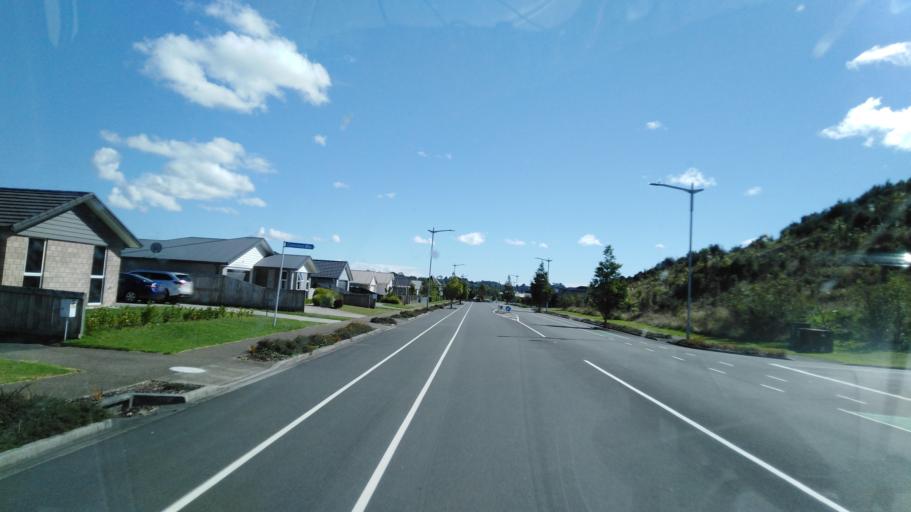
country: NZ
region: Bay of Plenty
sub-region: Tauranga City
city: Tauranga
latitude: -37.7585
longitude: 176.1038
